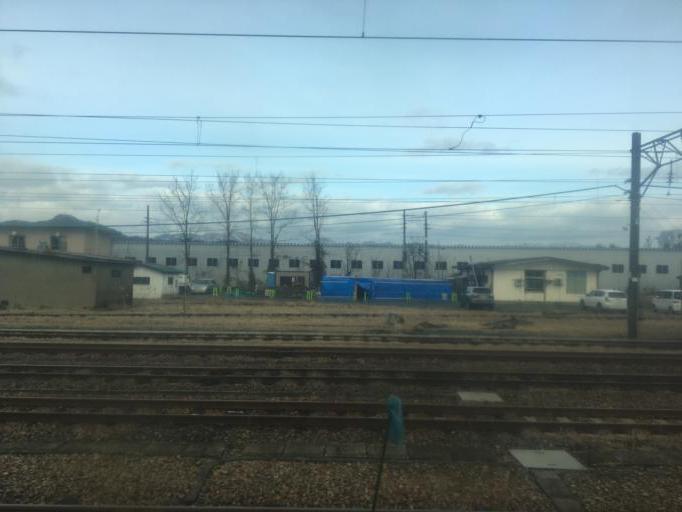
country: JP
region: Akita
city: Odate
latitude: 40.2885
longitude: 140.5579
